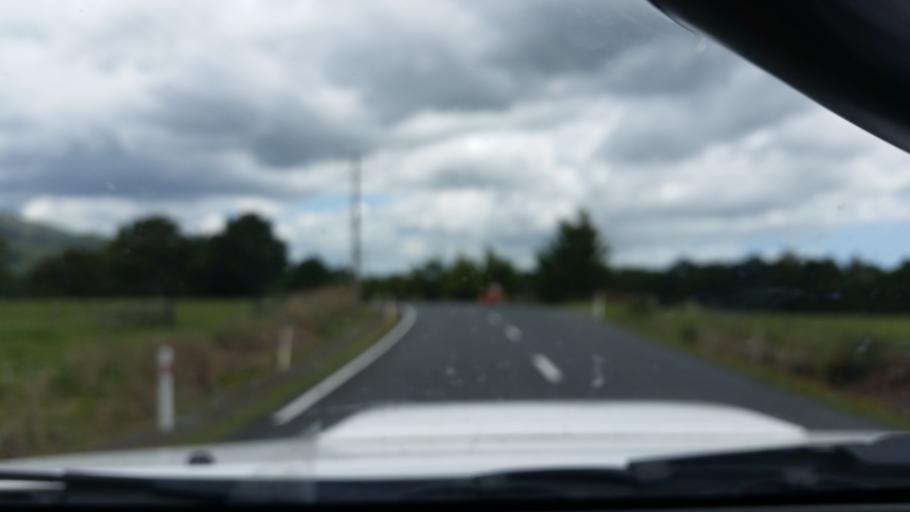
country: NZ
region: Northland
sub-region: Kaipara District
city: Dargaville
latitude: -35.7854
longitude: 173.9083
